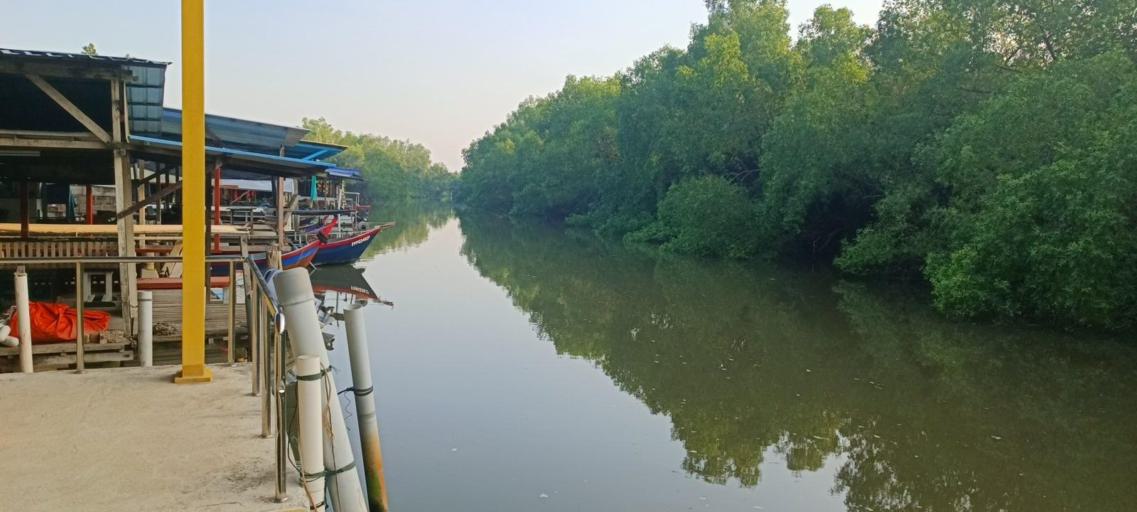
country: MY
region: Penang
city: Juru
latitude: 5.3376
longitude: 100.4159
